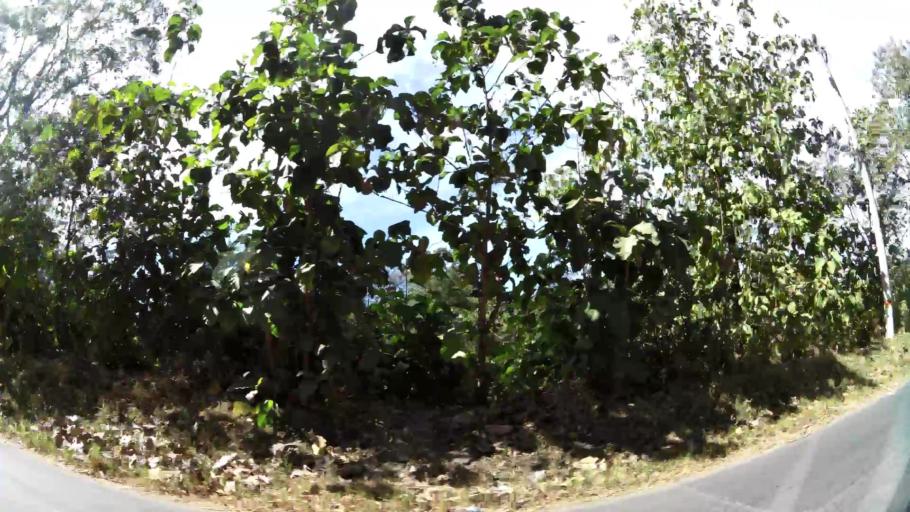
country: SV
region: San Salvador
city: Aguilares
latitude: 13.9625
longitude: -89.1666
